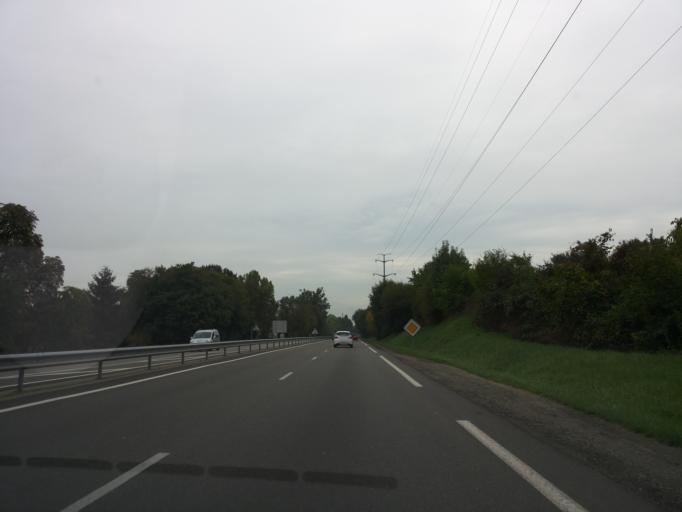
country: FR
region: Alsace
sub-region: Departement du Bas-Rhin
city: Eschau
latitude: 48.5090
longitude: 7.7301
